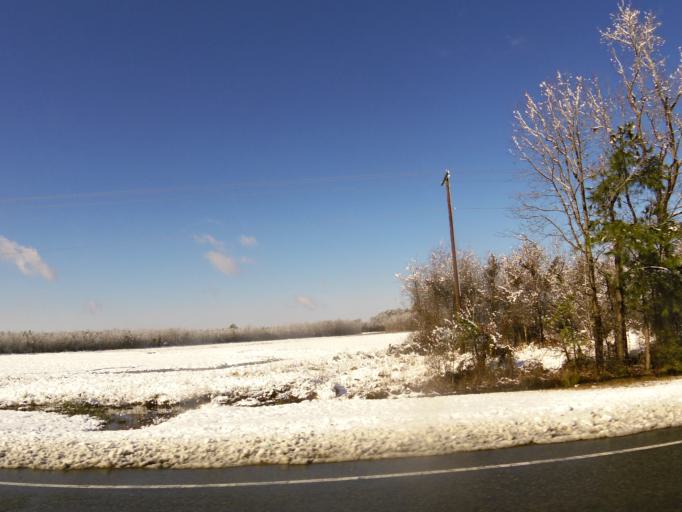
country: US
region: North Carolina
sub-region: Nash County
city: Sharpsburg
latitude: 35.8854
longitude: -77.8214
